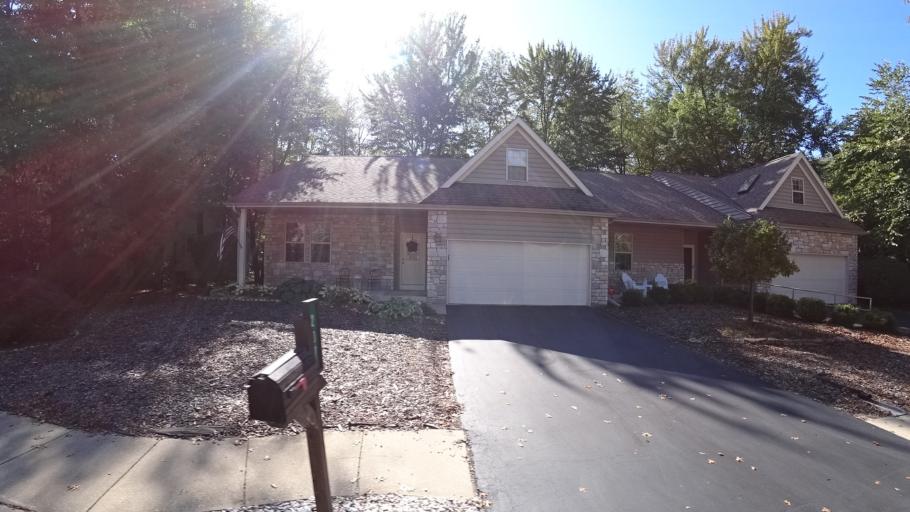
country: US
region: Indiana
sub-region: LaPorte County
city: Trail Creek
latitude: 41.6966
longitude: -86.8777
